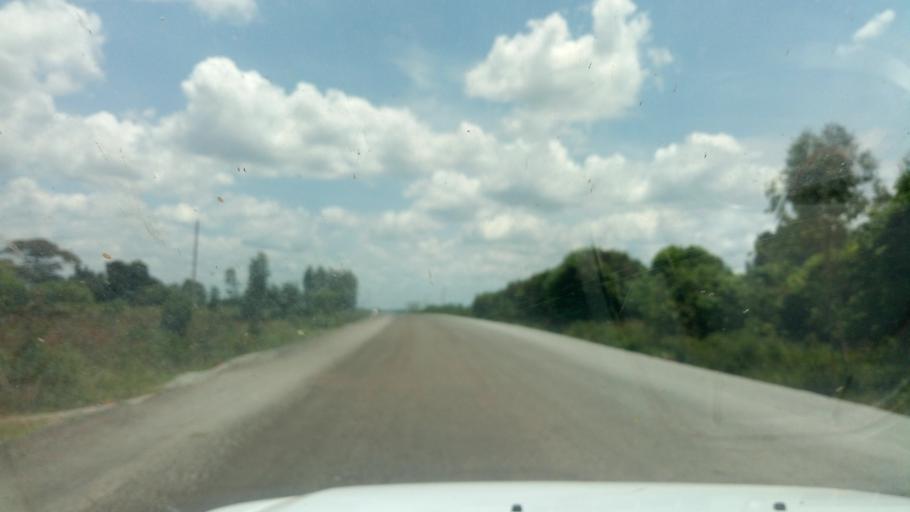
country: UG
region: Western Region
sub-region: Kiryandongo District
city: Kiryandongo
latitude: 1.7903
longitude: 31.9449
